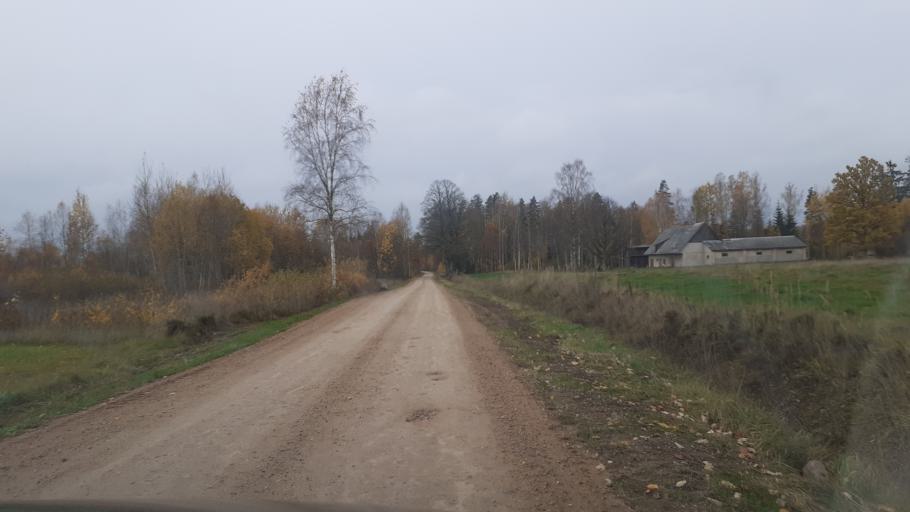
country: LV
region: Saldus Rajons
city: Saldus
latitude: 56.8752
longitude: 22.3150
